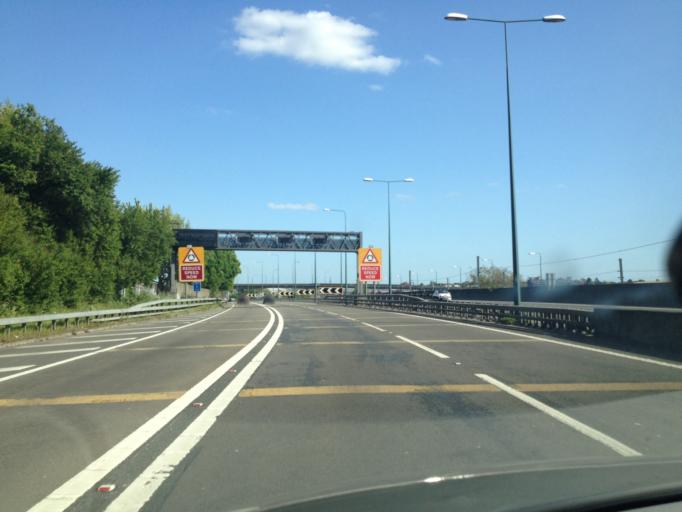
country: GB
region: England
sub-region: Greater London
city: Hendon
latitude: 51.5756
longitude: -0.2350
